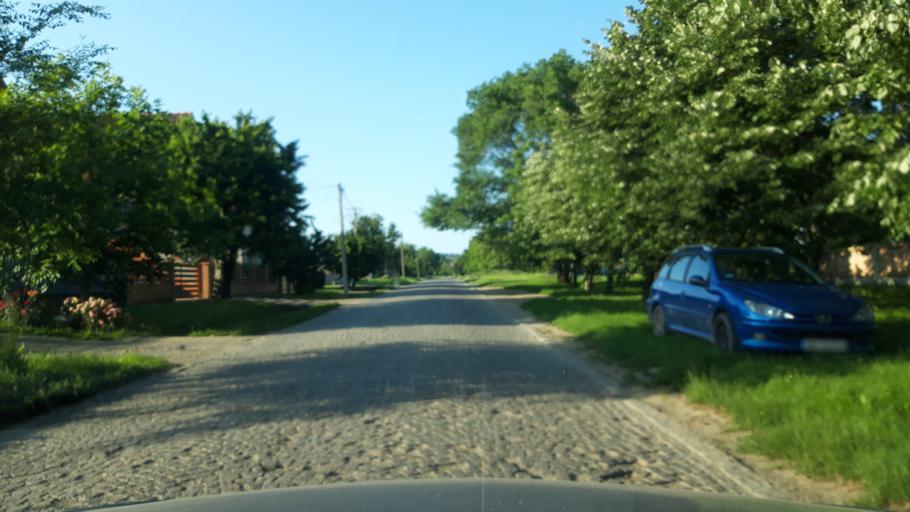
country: RS
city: Macvanska Mitrovica
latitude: 45.1048
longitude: 19.5021
